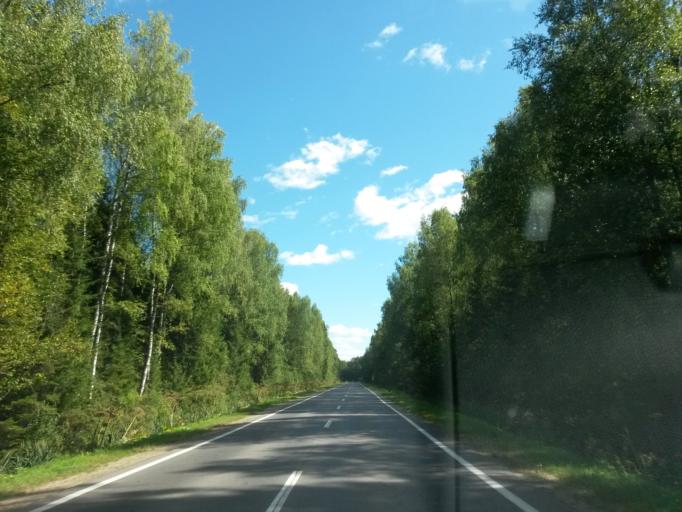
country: RU
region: Jaroslavl
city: Yaroslavl
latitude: 57.8017
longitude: 39.7916
